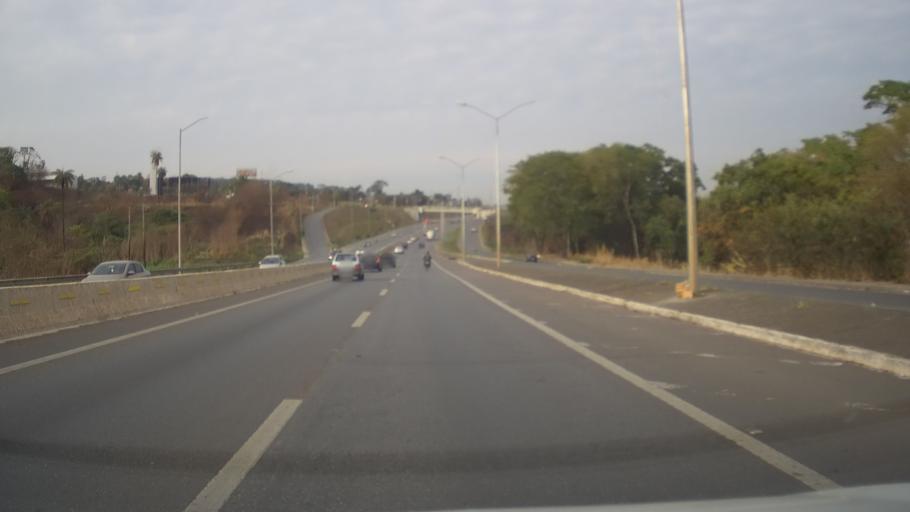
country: BR
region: Minas Gerais
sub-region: Vespasiano
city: Vespasiano
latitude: -19.7185
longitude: -43.9301
